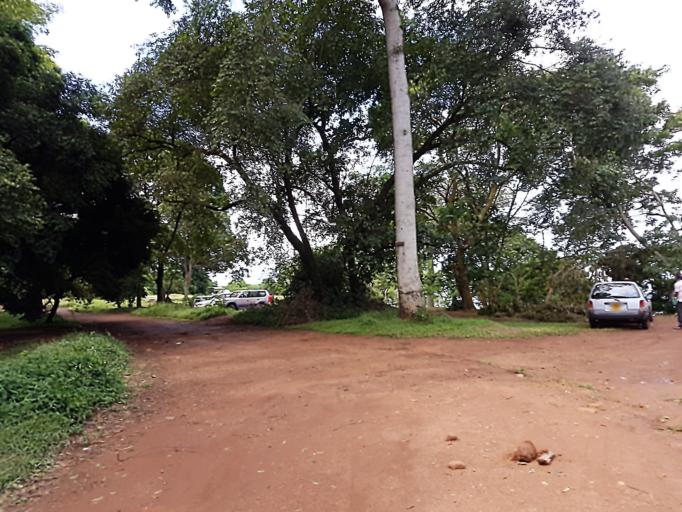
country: UG
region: Central Region
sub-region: Wakiso District
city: Entebbe
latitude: 0.0593
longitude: 32.4810
